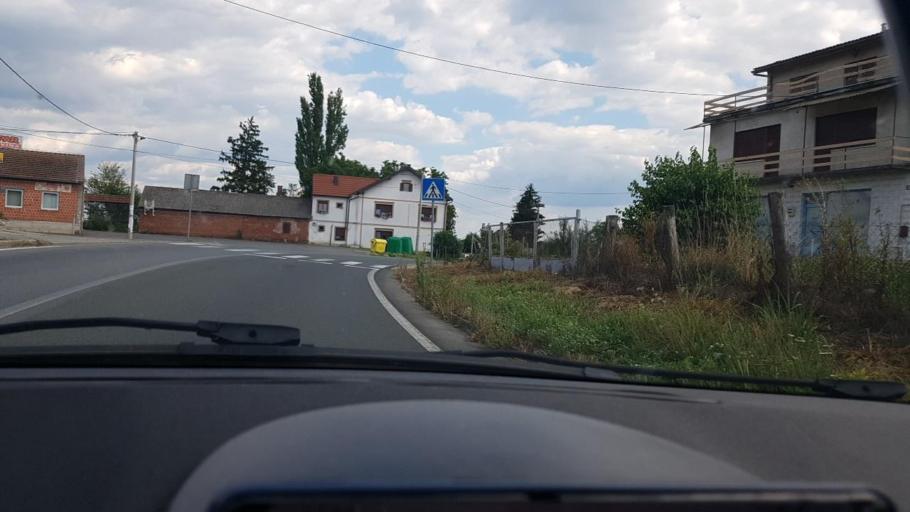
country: HR
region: Bjelovarsko-Bilogorska
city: Zdralovi
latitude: 45.8643
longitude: 16.9182
